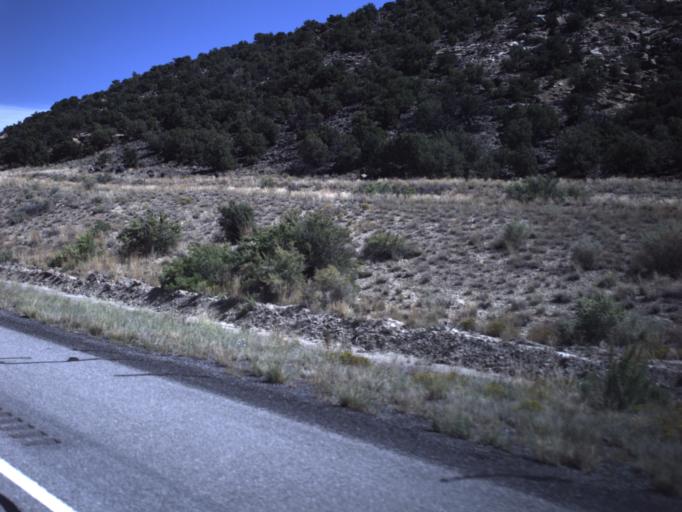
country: US
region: Utah
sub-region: Emery County
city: Ferron
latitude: 38.7985
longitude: -111.2797
